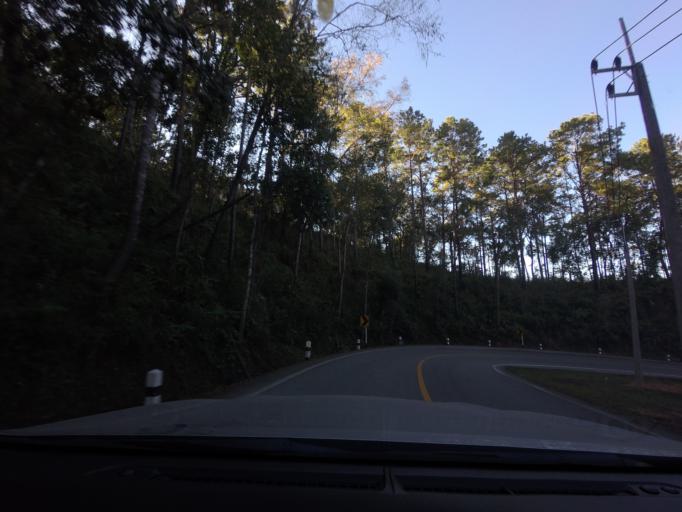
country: TH
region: Mae Hong Son
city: Mae Hi
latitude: 19.2716
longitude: 98.5774
